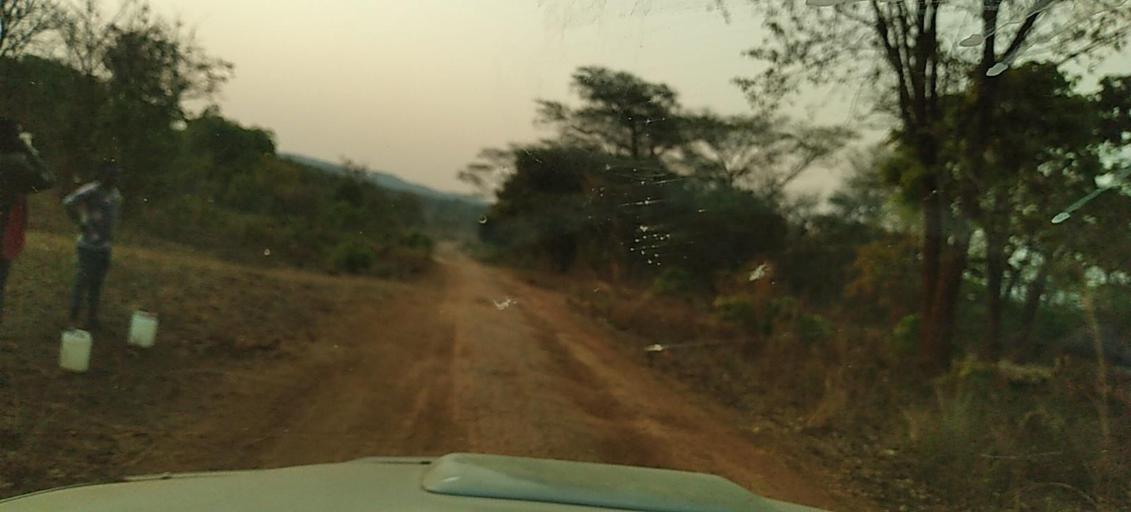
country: ZM
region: North-Western
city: Kasempa
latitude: -13.0725
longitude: 26.3843
